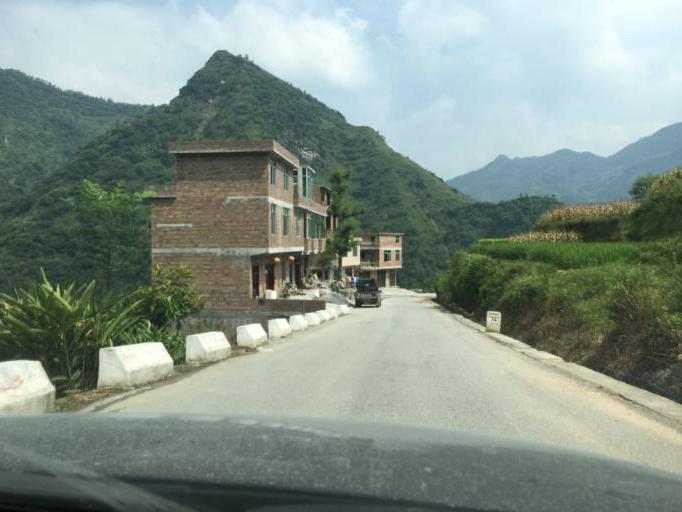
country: CN
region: Guangxi Zhuangzu Zizhiqu
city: Tongle
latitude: 25.2969
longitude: 106.2656
